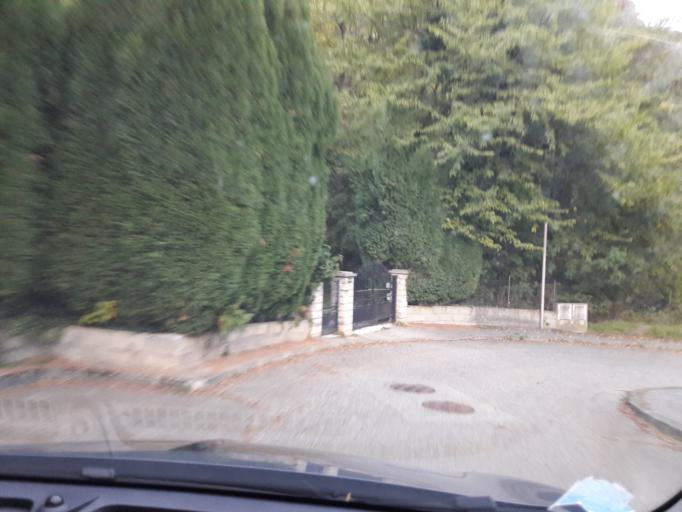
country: FR
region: Rhone-Alpes
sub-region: Departement de la Savoie
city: Saint-Jean-de-Maurienne
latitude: 45.3088
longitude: 6.3490
